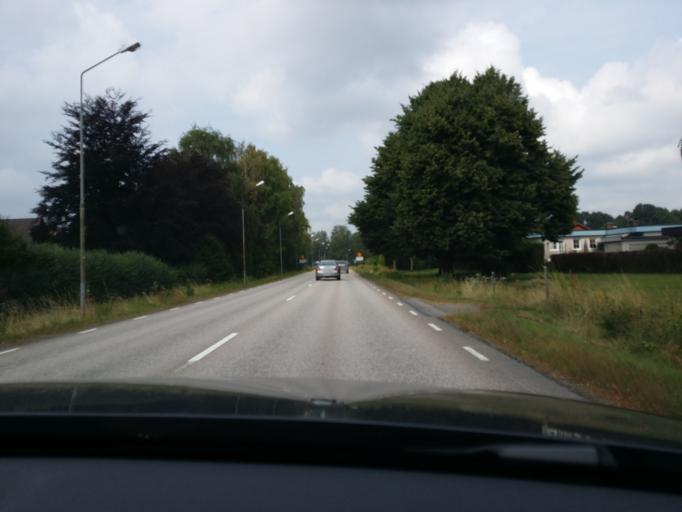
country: SE
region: Blekinge
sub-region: Karlshamns Kommun
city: Morrum
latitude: 56.1899
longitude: 14.7584
